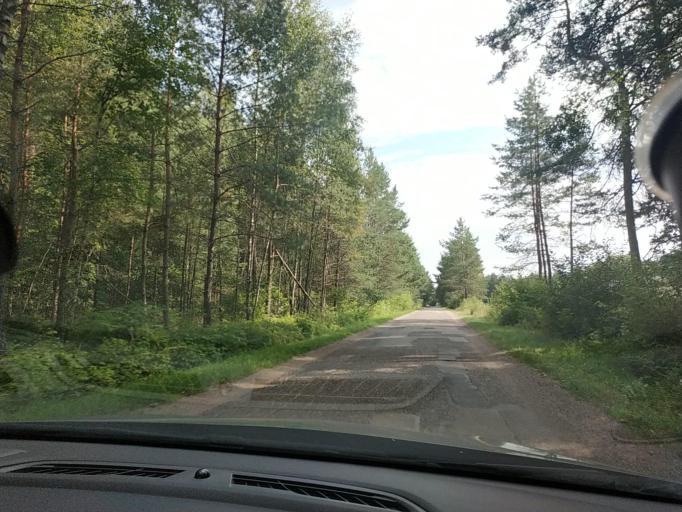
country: LT
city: Nemencine
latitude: 54.8509
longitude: 25.4509
